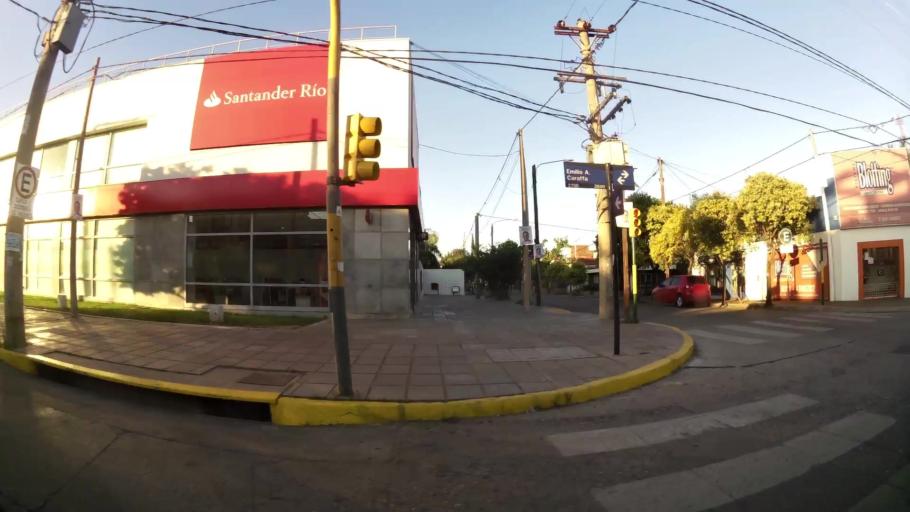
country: AR
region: Cordoba
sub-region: Departamento de Capital
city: Cordoba
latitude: -31.3874
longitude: -64.2140
